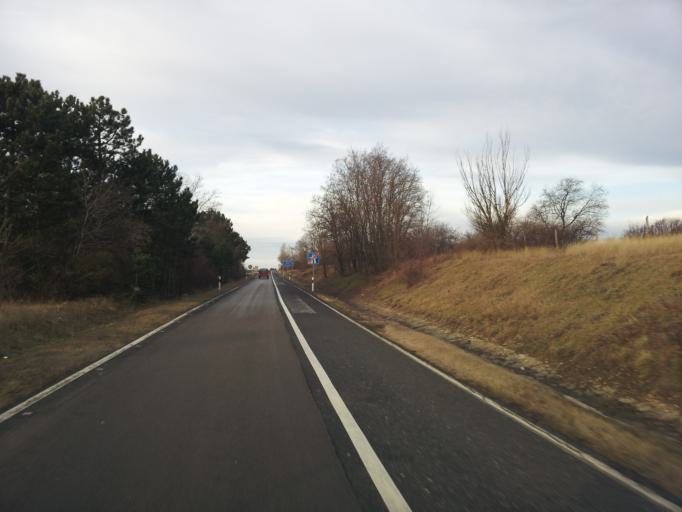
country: HU
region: Fejer
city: Lepseny
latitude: 46.9933
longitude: 18.1902
